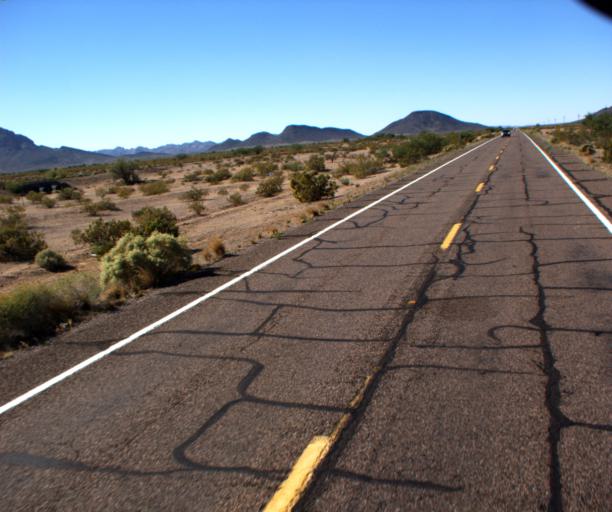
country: US
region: Arizona
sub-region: Maricopa County
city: Gila Bend
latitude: 32.7986
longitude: -112.8004
